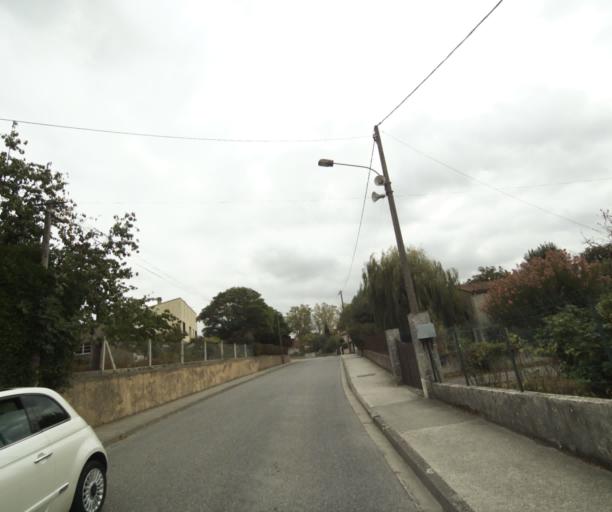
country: FR
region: Midi-Pyrenees
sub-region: Departement de la Haute-Garonne
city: Villefranche-de-Lauragais
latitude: 43.4038
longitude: 1.7180
